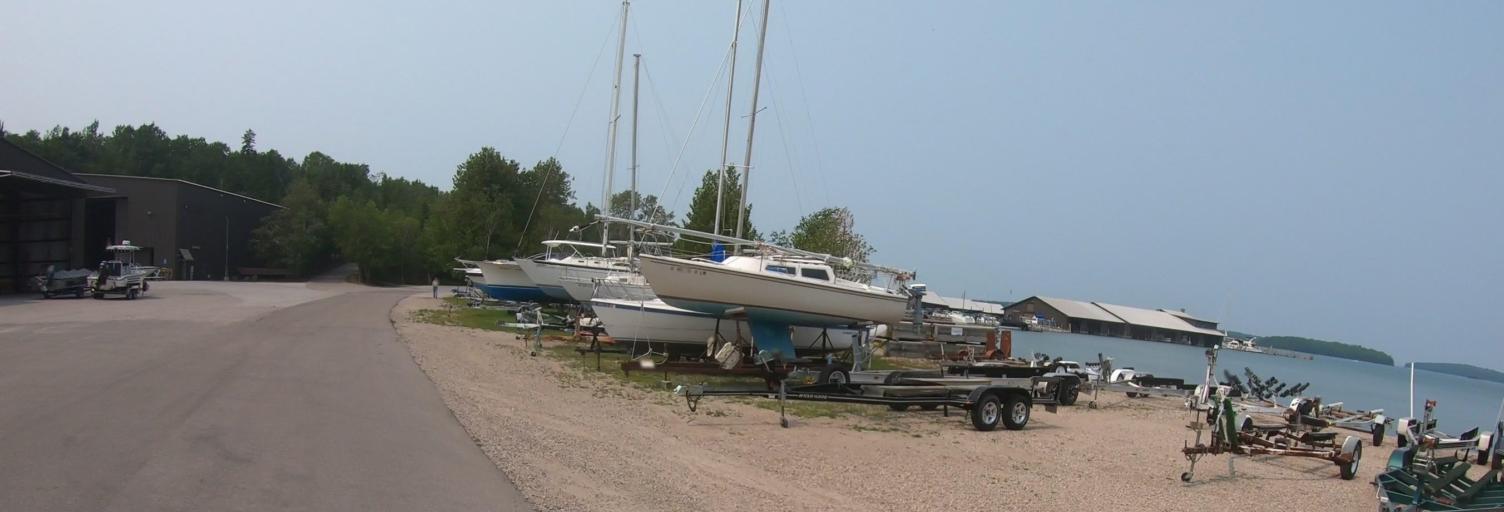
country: CA
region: Ontario
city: Thessalon
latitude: 46.0224
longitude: -83.7481
